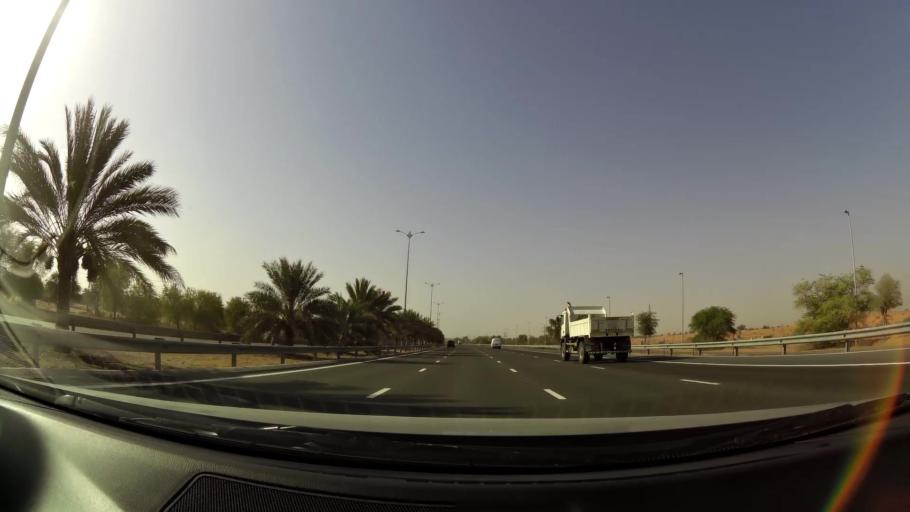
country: OM
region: Al Buraimi
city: Al Buraymi
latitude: 24.6023
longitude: 55.7323
